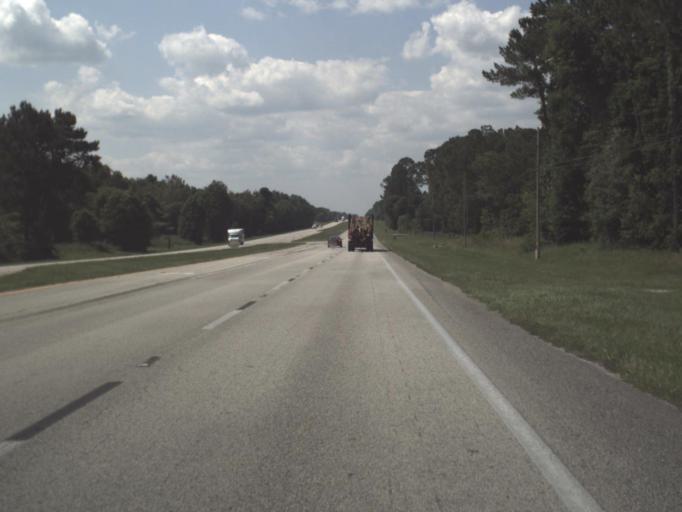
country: US
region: Florida
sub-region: Alachua County
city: Hawthorne
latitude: 29.6316
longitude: -82.1021
